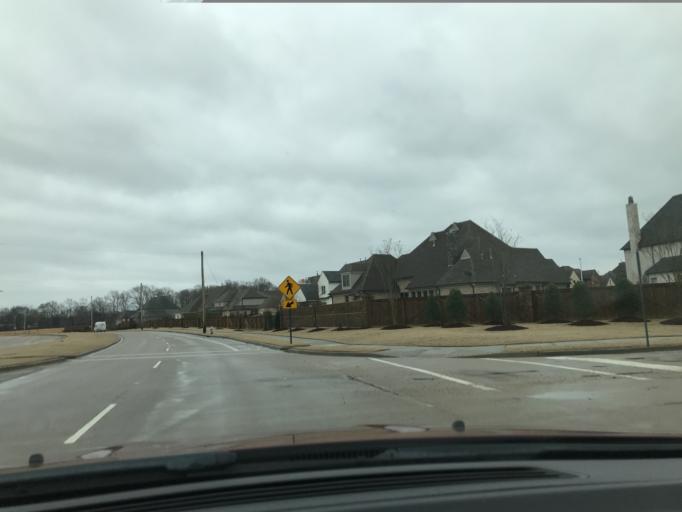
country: US
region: Tennessee
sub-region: Shelby County
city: Collierville
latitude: 35.0877
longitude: -89.7064
